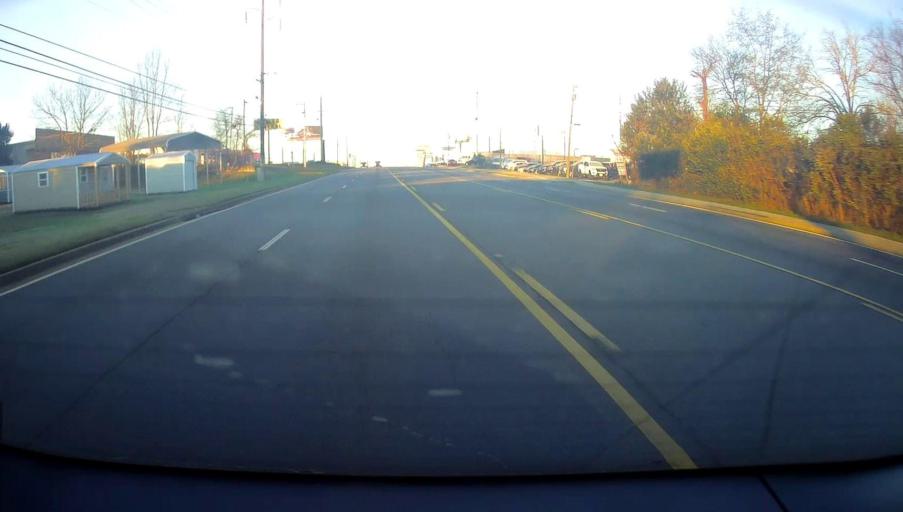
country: US
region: Georgia
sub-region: Houston County
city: Centerville
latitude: 32.6188
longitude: -83.6639
